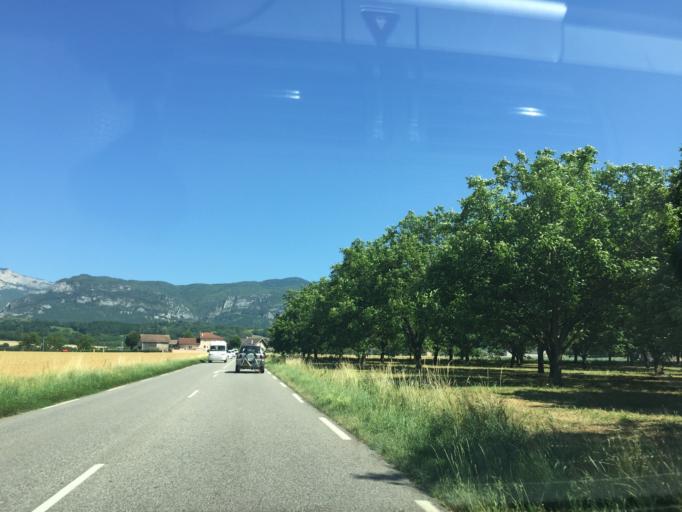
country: FR
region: Rhone-Alpes
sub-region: Departement de l'Isere
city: Saint-Just-de-Claix
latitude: 45.0535
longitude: 5.2893
